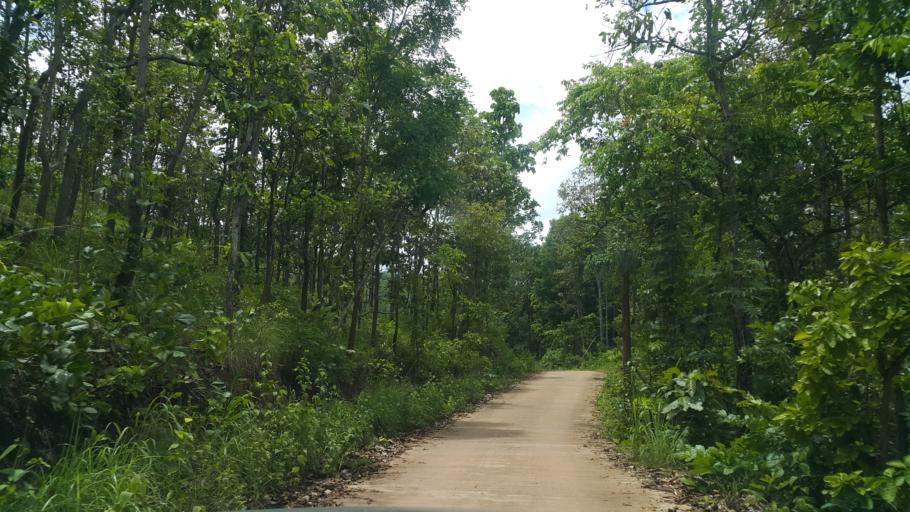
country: TH
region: Chiang Mai
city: Mae Taeng
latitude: 19.2274
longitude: 99.0069
